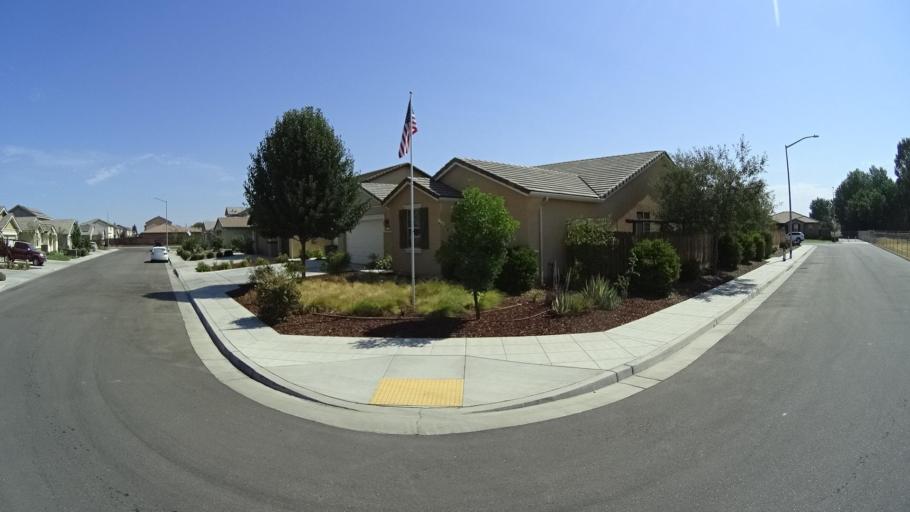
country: US
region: California
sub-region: Fresno County
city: Sunnyside
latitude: 36.7686
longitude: -119.6610
